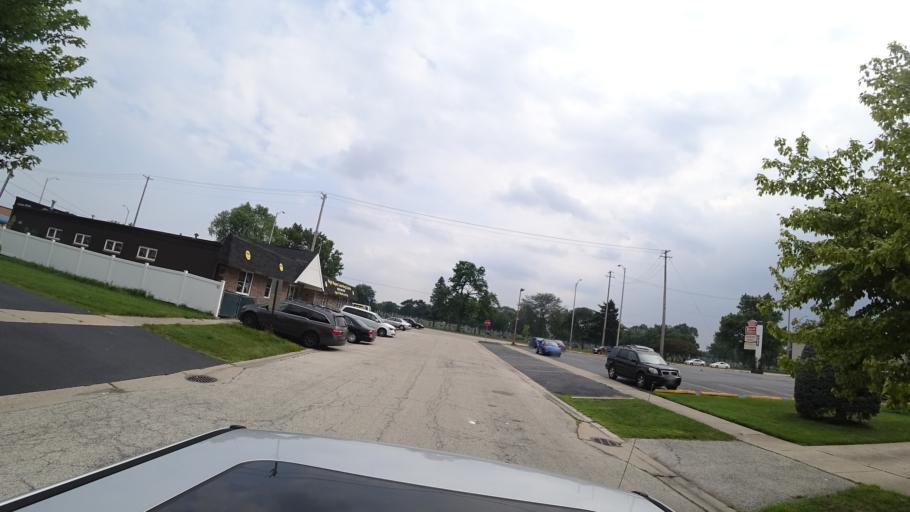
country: US
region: Illinois
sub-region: Cook County
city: Chicago Ridge
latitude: 41.6910
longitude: -87.7752
